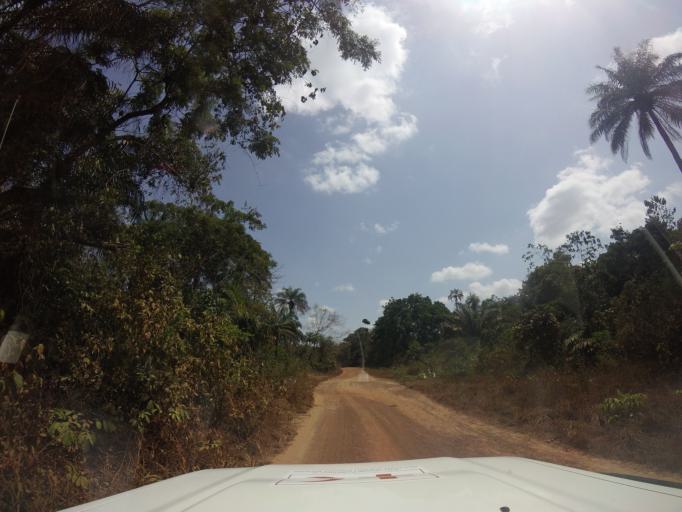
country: SL
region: Southern Province
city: Zimmi
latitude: 7.0351
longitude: -11.2837
